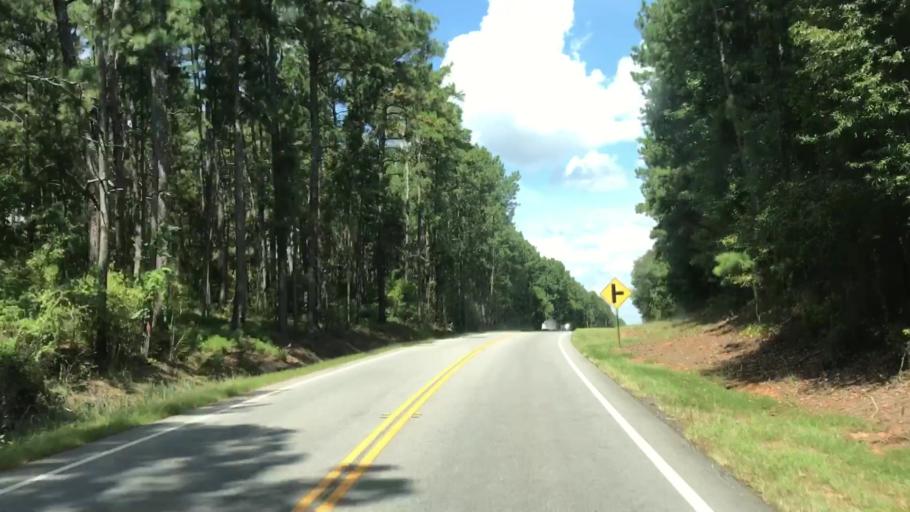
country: US
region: Georgia
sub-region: Greene County
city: Greensboro
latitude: 33.6806
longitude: -83.2715
